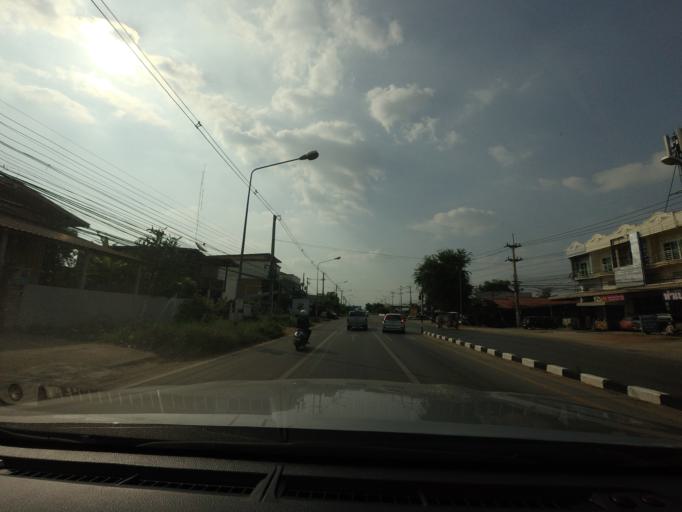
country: TH
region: Sukhothai
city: Sukhothai
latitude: 17.0105
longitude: 99.7885
